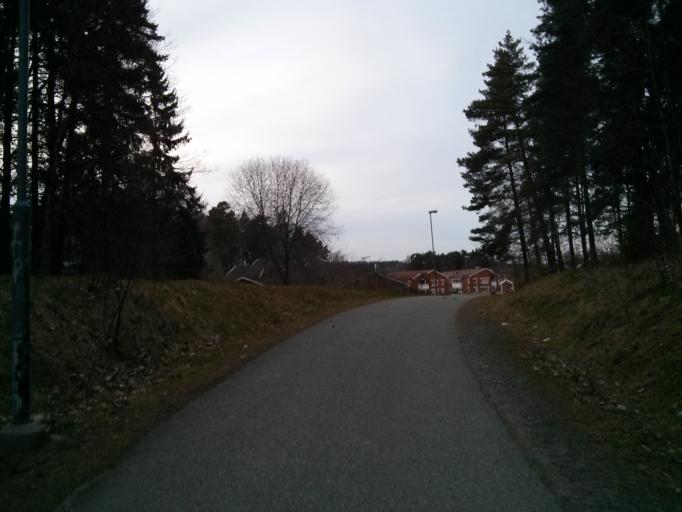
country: SE
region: Stockholm
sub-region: Upplands Vasby Kommun
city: Upplands Vaesby
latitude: 59.5096
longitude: 17.8847
